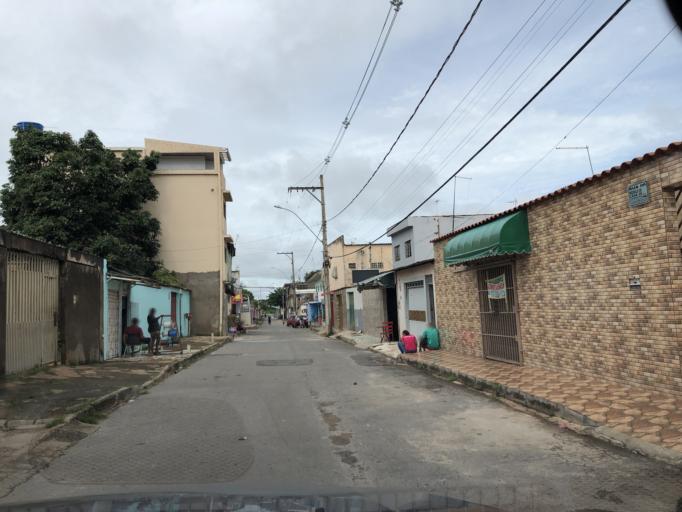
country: BR
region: Federal District
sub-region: Brasilia
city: Brasilia
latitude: -15.7829
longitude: -48.1390
